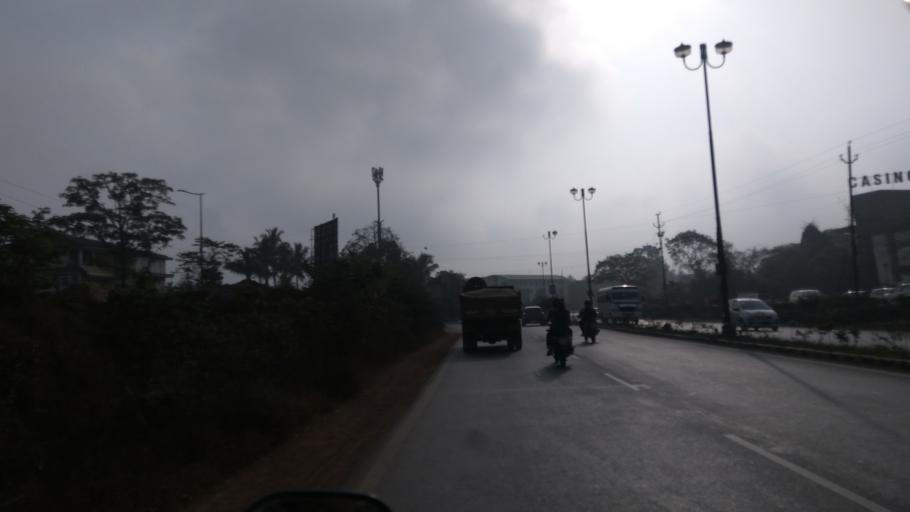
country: IN
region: Goa
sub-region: North Goa
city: Panaji
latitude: 15.5174
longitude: 73.8321
